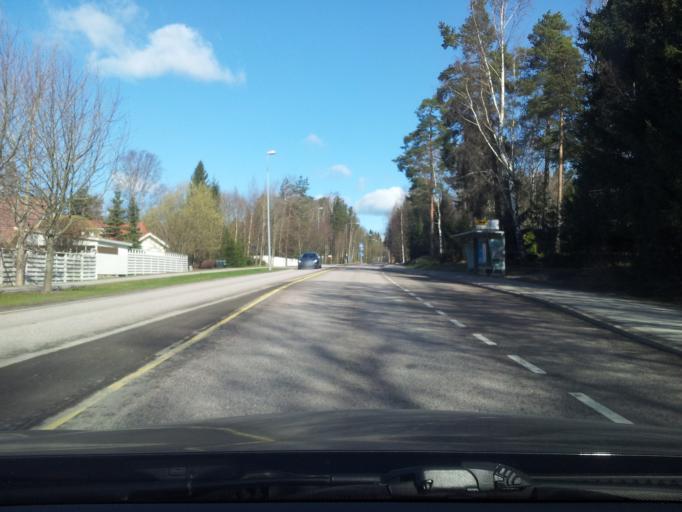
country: FI
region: Uusimaa
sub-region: Helsinki
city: Espoo
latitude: 60.1815
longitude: 24.6707
